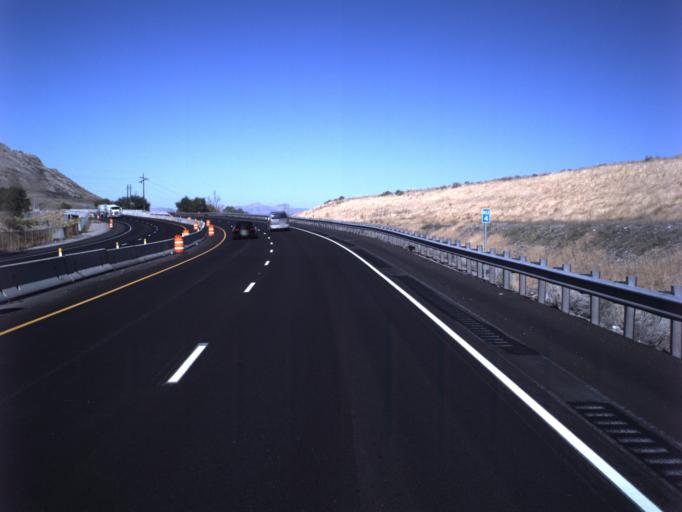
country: US
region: Utah
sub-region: Salt Lake County
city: Magna
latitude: 40.7207
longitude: -112.1505
